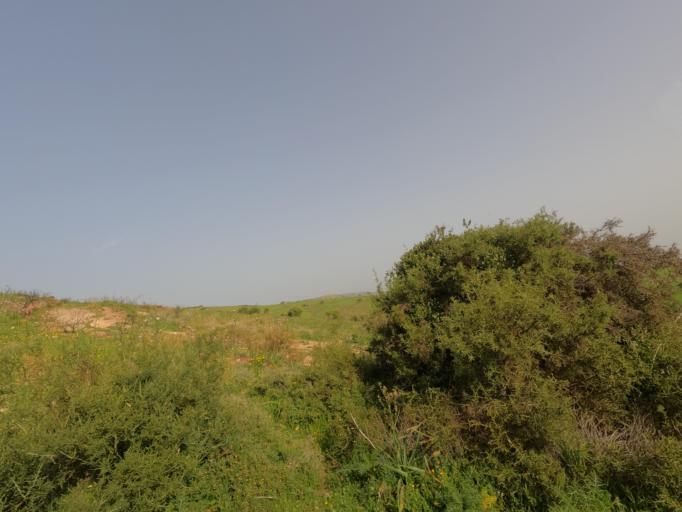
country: CY
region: Pafos
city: Polis
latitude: 34.9980
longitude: 32.3599
